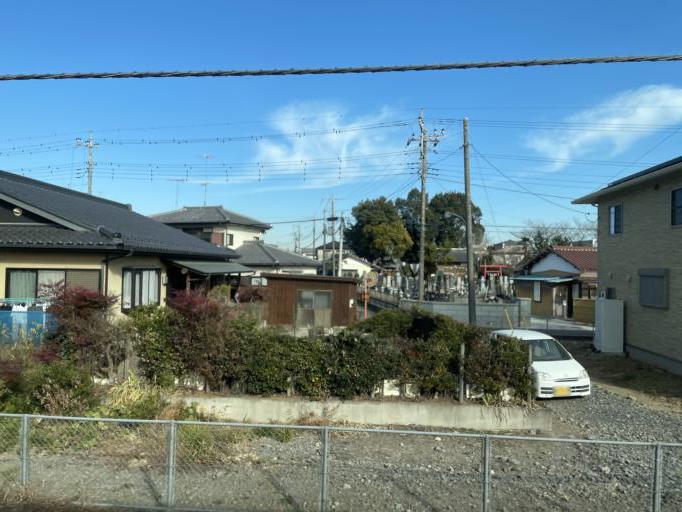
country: JP
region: Saitama
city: Fukiage-fujimi
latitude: 36.1055
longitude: 139.4434
